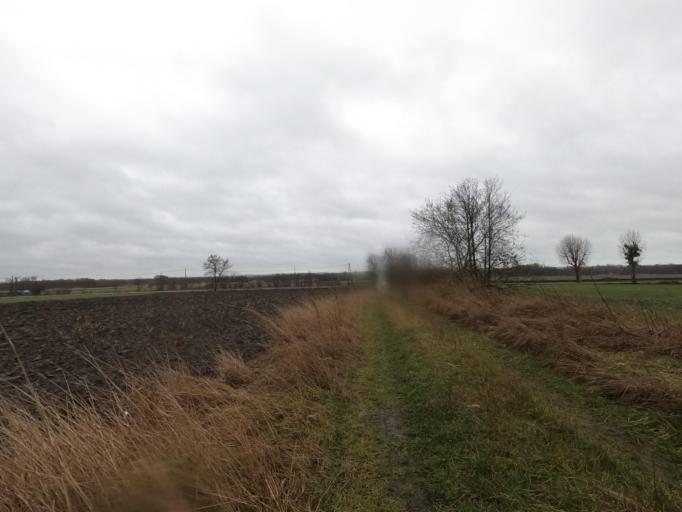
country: PL
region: Greater Poland Voivodeship
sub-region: Powiat pilski
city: Osiek nad Notecia
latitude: 53.1160
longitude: 17.2616
